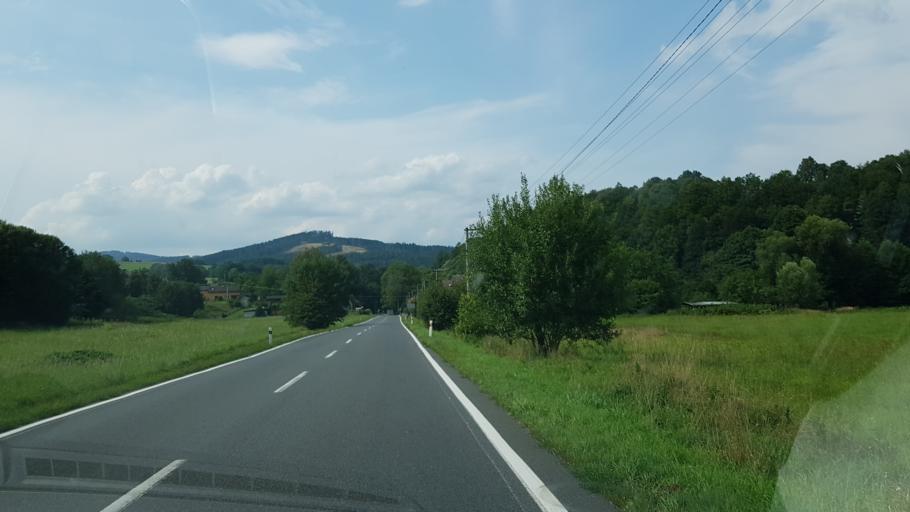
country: CZ
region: Olomoucky
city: Zlate Hory
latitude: 50.2636
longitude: 17.3577
